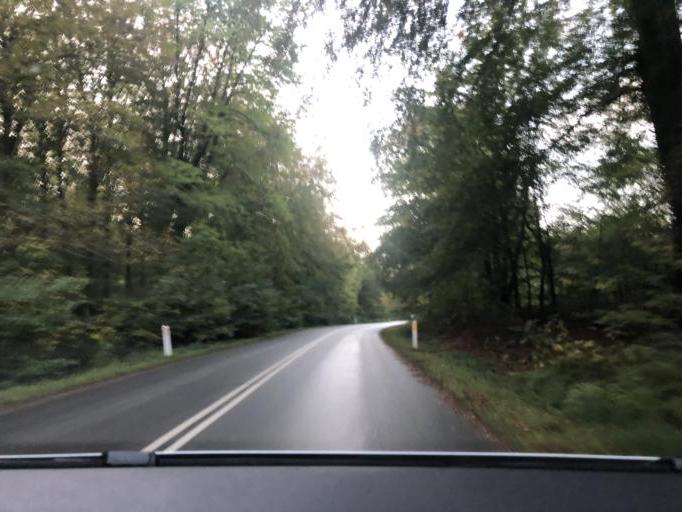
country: DK
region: Capital Region
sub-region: Frederikssund Kommune
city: Slangerup
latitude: 55.8154
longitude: 12.2042
